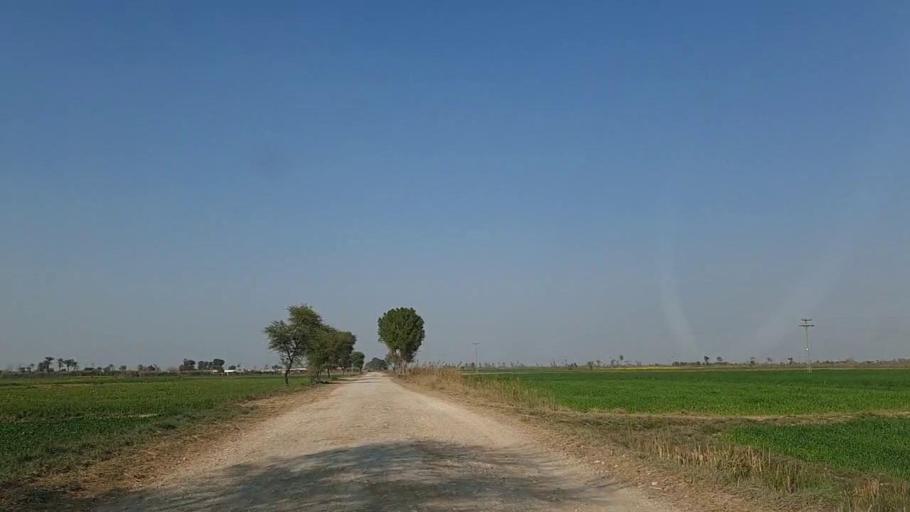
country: PK
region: Sindh
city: Daur
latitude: 26.4734
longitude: 68.2970
